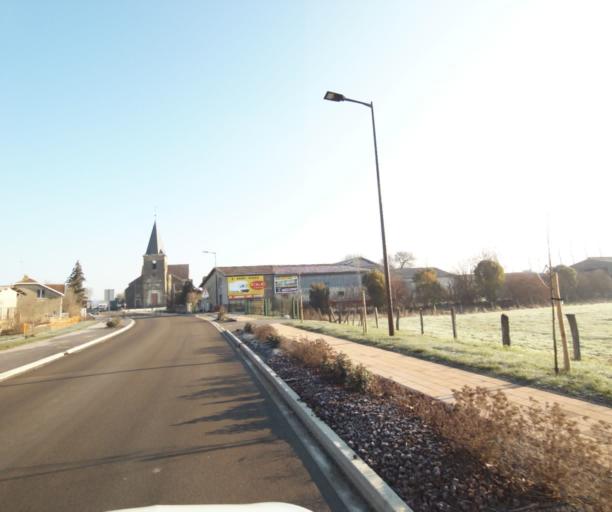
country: FR
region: Champagne-Ardenne
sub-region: Departement de la Haute-Marne
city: Montier-en-Der
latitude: 48.4335
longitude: 4.7237
